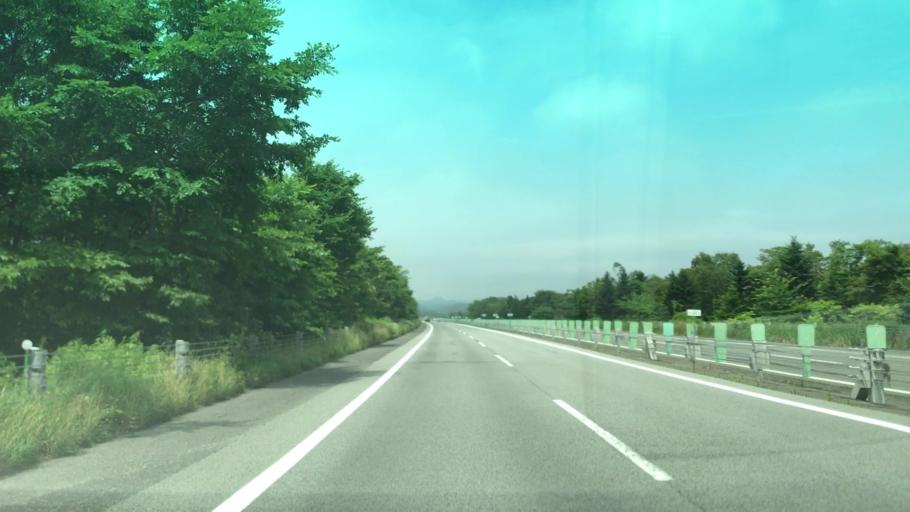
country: JP
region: Hokkaido
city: Shiraoi
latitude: 42.5148
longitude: 141.2697
